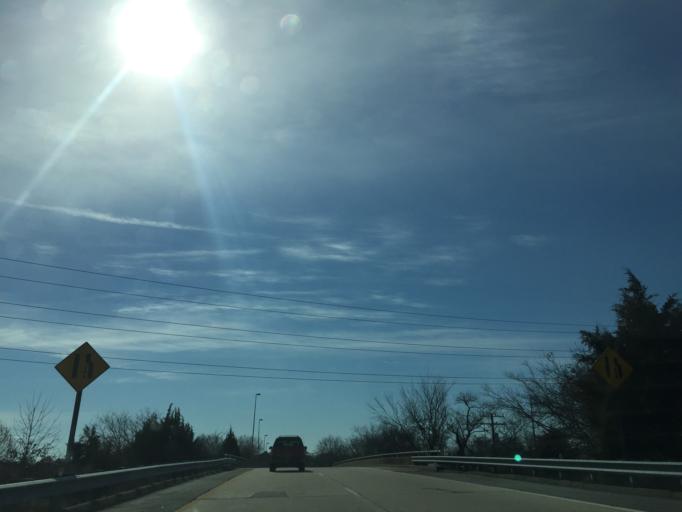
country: US
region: Virginia
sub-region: City of Norfolk
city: Norfolk
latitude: 36.9057
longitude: -76.2580
